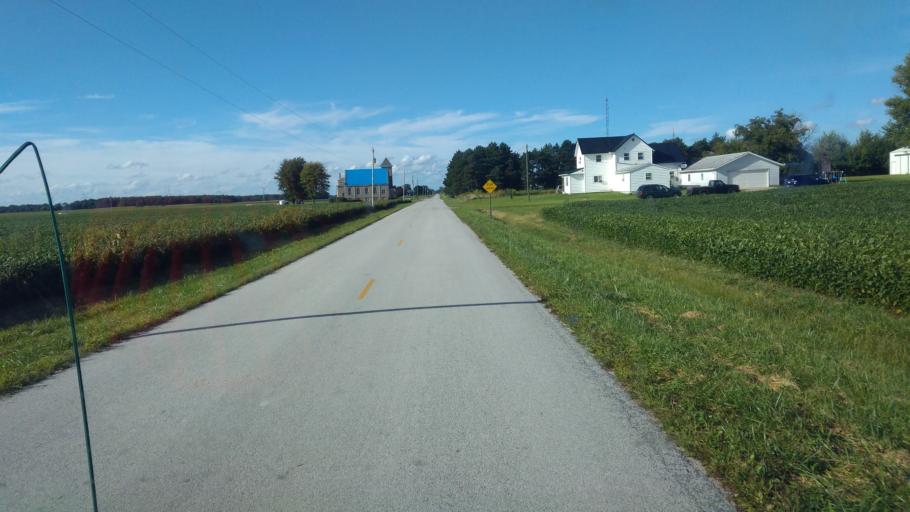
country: US
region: Ohio
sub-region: Hardin County
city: Kenton
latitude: 40.7439
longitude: -83.6906
